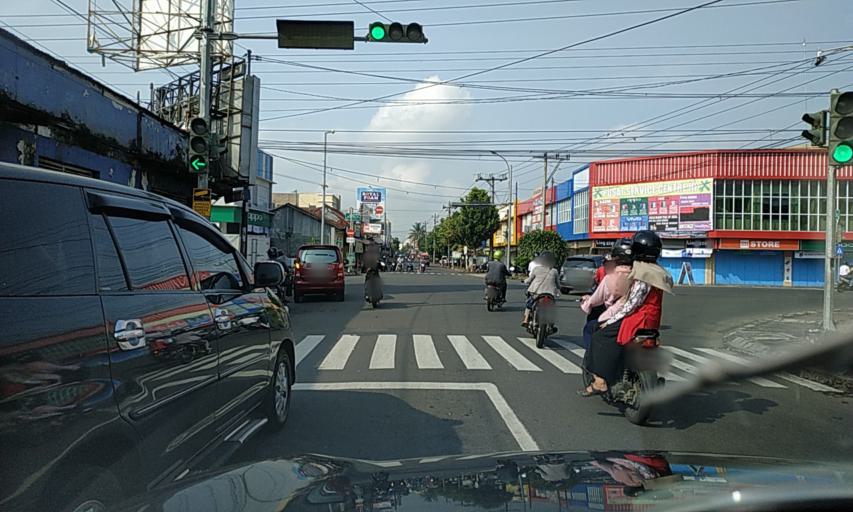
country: ID
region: Central Java
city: Purwokerto
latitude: -7.4230
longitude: 109.2440
